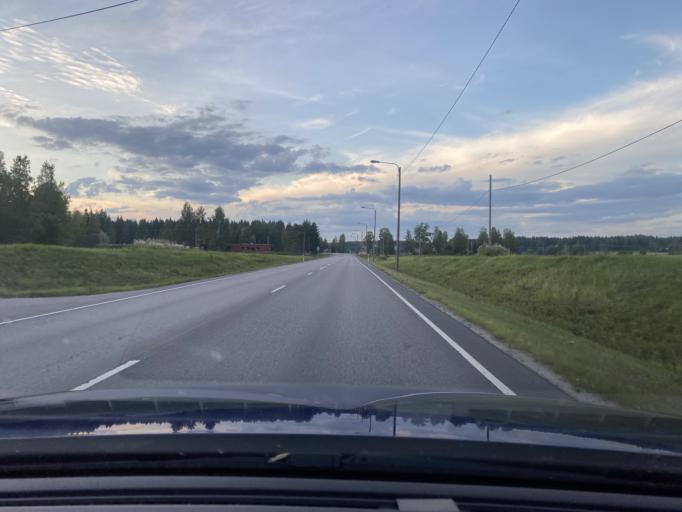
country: FI
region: Satakunta
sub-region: Pohjois-Satakunta
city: Kankaanpaeae
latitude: 61.7403
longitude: 22.5251
